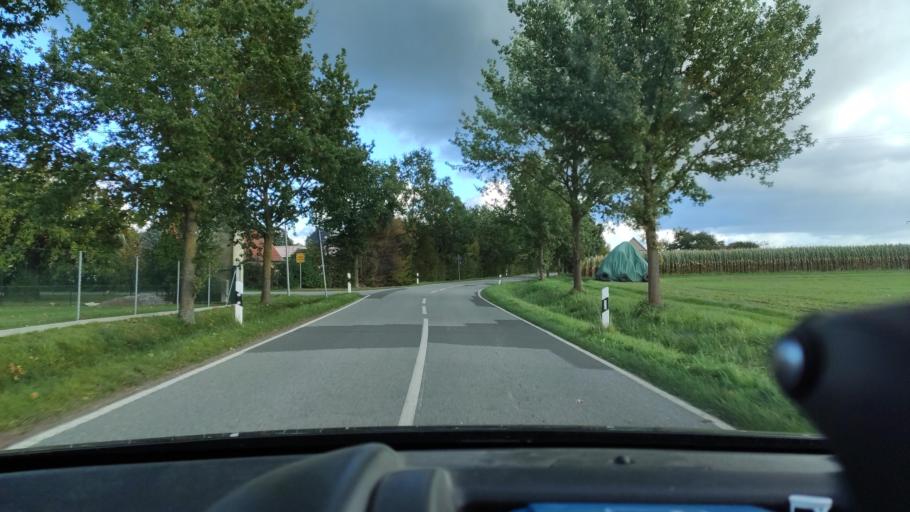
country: DE
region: Mecklenburg-Vorpommern
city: Butzow
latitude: 53.8017
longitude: 11.9586
